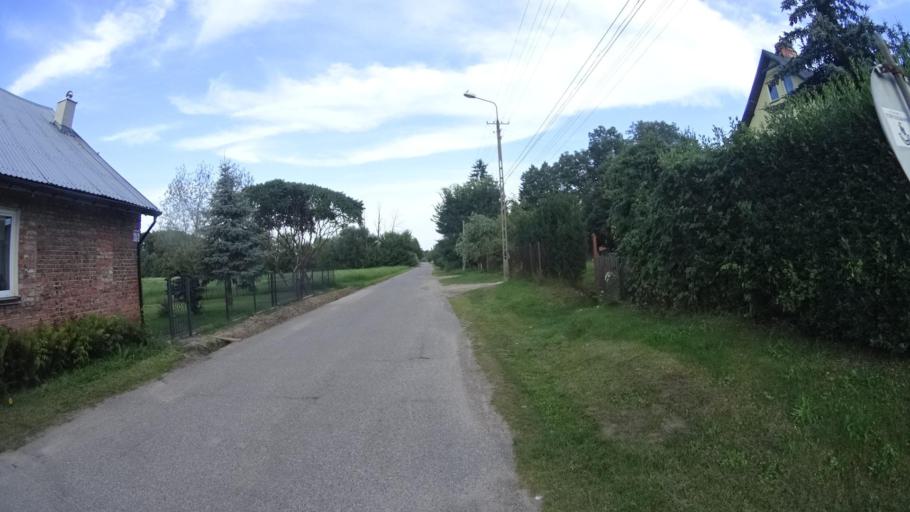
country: PL
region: Masovian Voivodeship
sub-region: Powiat piaseczynski
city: Tarczyn
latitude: 51.9764
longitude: 20.8486
